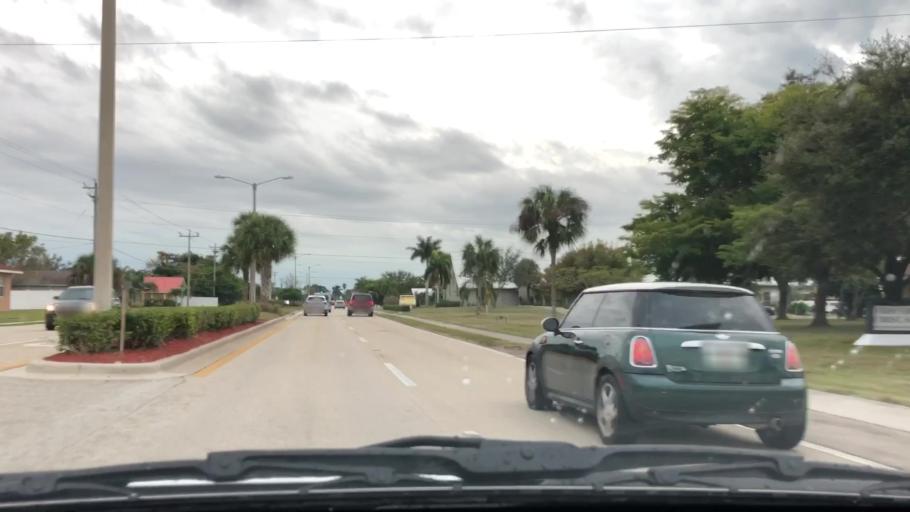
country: US
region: Florida
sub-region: Lee County
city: Cape Coral
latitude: 26.6041
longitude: -81.9565
